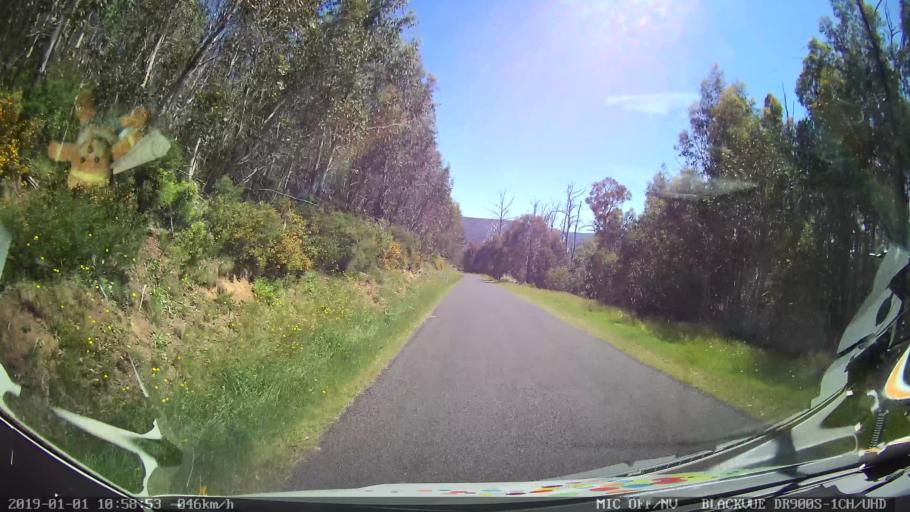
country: AU
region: New South Wales
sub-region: Snowy River
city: Jindabyne
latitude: -35.9893
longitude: 148.3985
